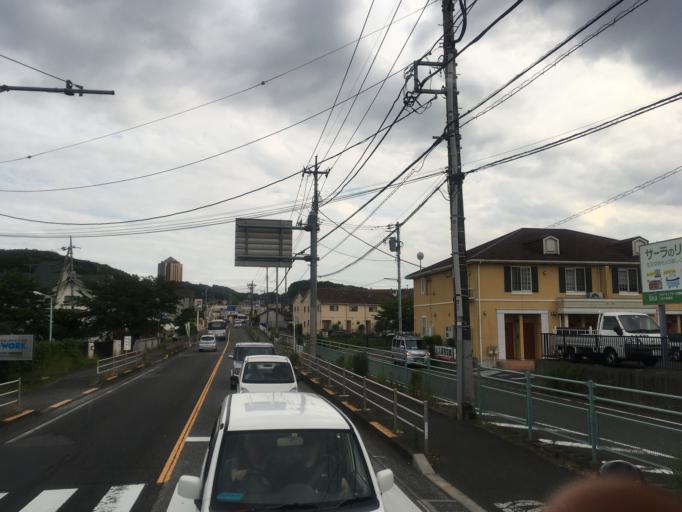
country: JP
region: Tokyo
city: Hachioji
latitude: 35.6382
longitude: 139.3395
